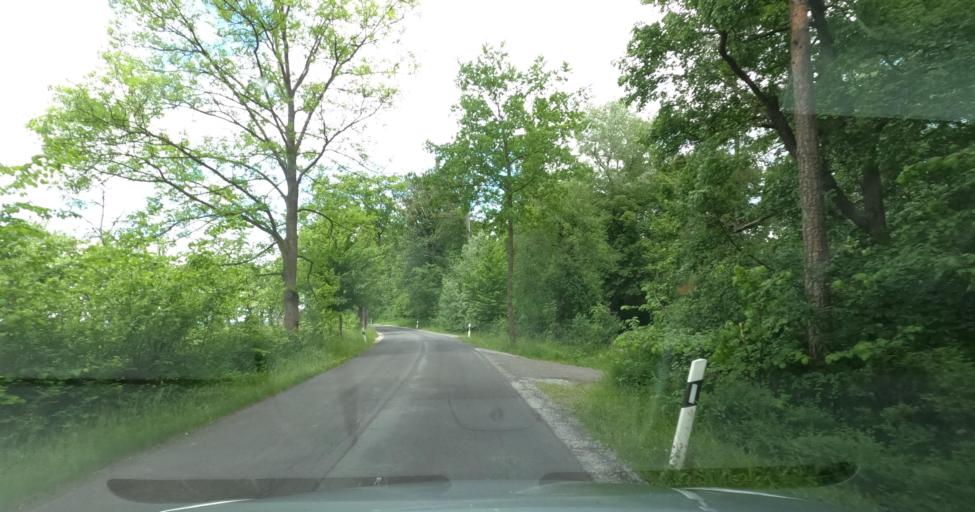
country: DE
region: Thuringia
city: Vollersroda
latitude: 50.9453
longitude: 11.3467
